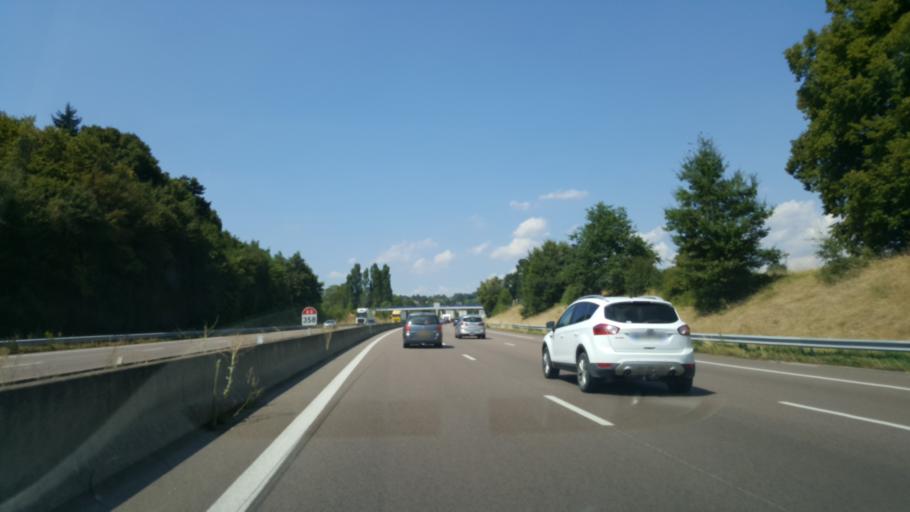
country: FR
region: Bourgogne
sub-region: Departement de Saone-et-Loire
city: Tournus
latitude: 46.5577
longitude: 4.8993
